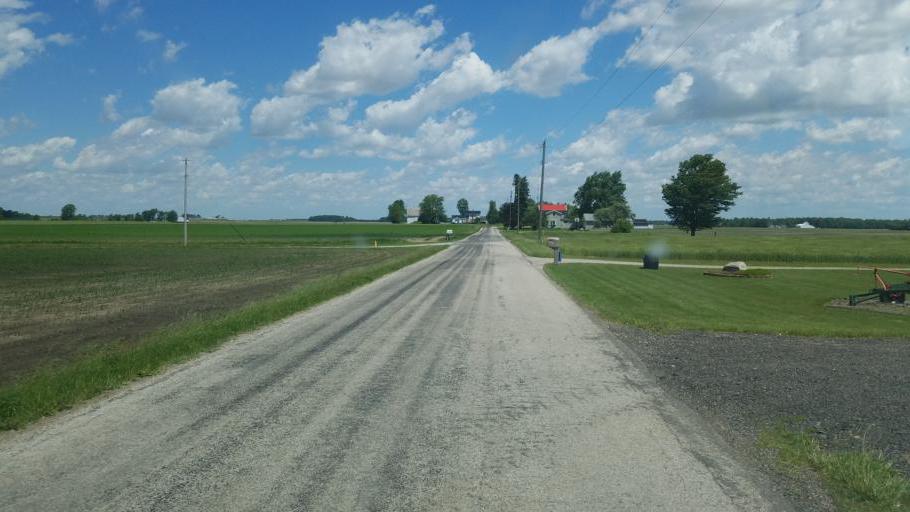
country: US
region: Ohio
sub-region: Richland County
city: Shelby
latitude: 40.8975
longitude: -82.7053
